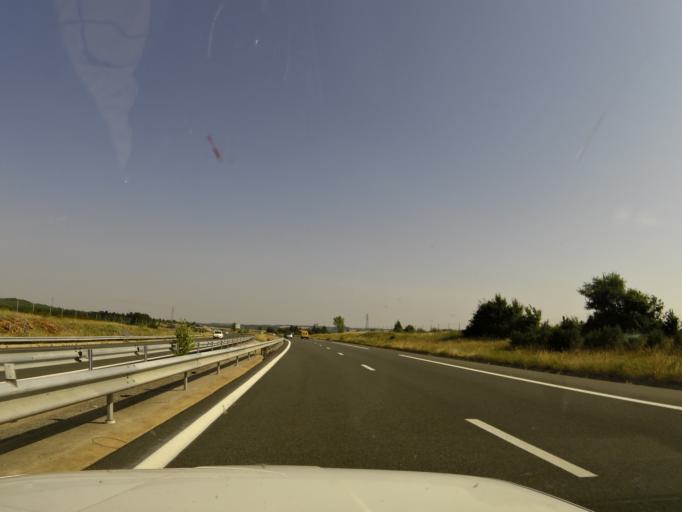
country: FR
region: Midi-Pyrenees
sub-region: Departement de l'Aveyron
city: La Cavalerie
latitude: 43.9578
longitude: 3.2108
